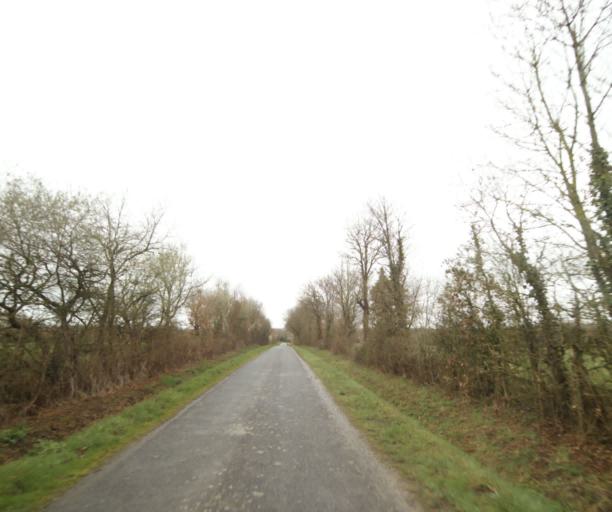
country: FR
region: Pays de la Loire
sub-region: Departement de la Loire-Atlantique
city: Bouvron
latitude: 47.4569
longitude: -1.8783
